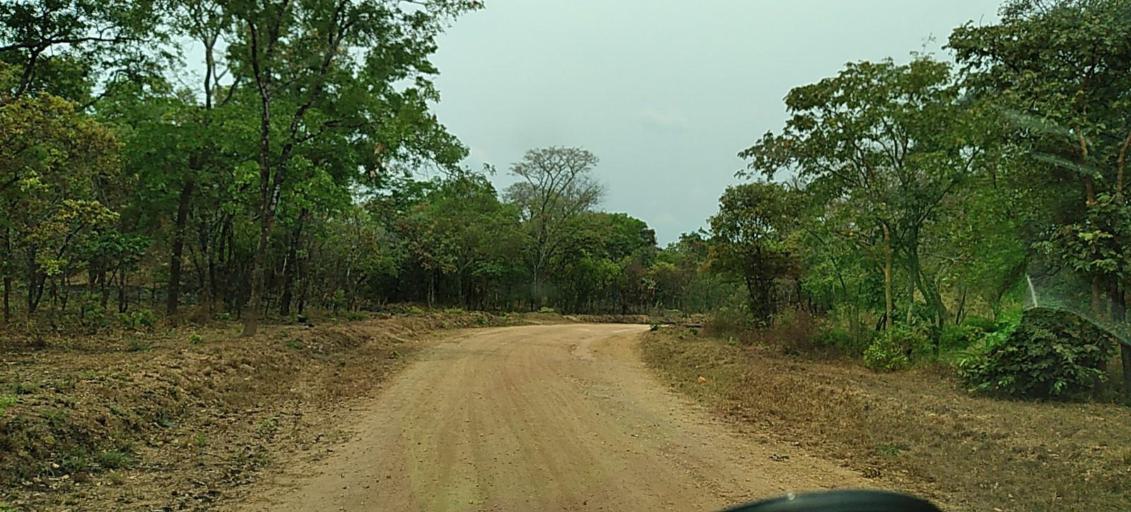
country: ZM
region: North-Western
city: Solwezi
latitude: -12.7829
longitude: 26.5205
